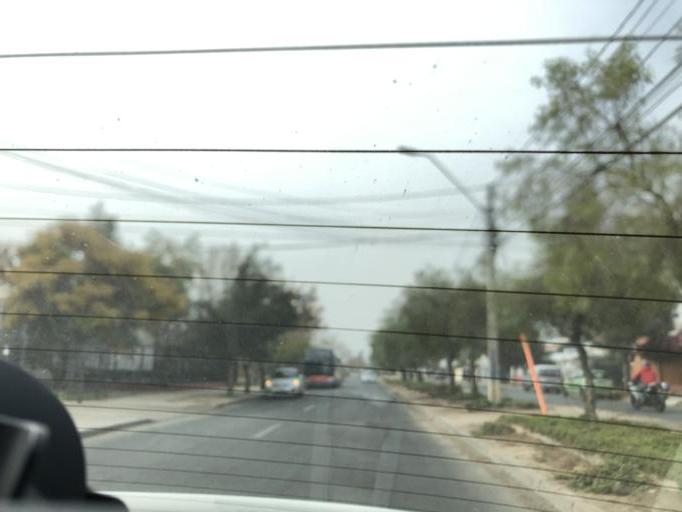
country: CL
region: Santiago Metropolitan
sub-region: Provincia de Cordillera
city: Puente Alto
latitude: -33.5926
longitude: -70.5640
